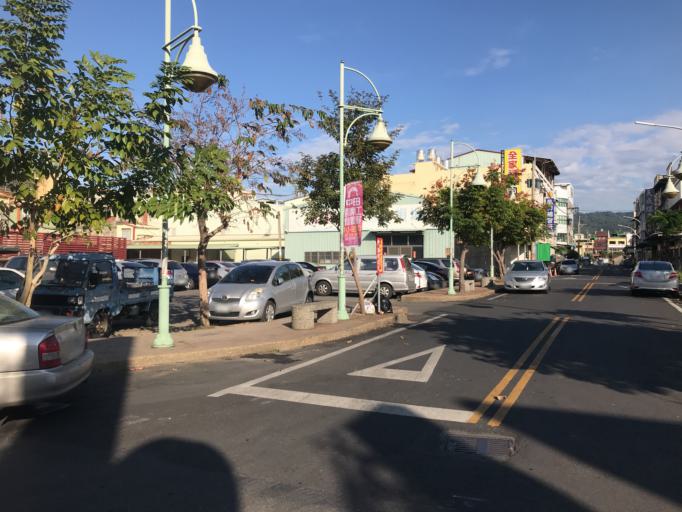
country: TW
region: Taiwan
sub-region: Nantou
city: Nantou
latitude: 23.8987
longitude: 120.5887
